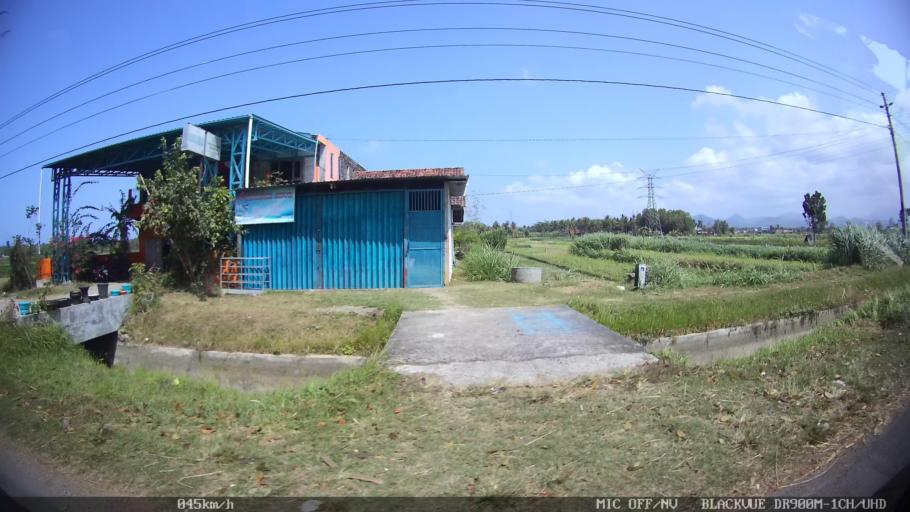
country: ID
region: Daerah Istimewa Yogyakarta
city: Srandakan
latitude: -7.9006
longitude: 110.1525
